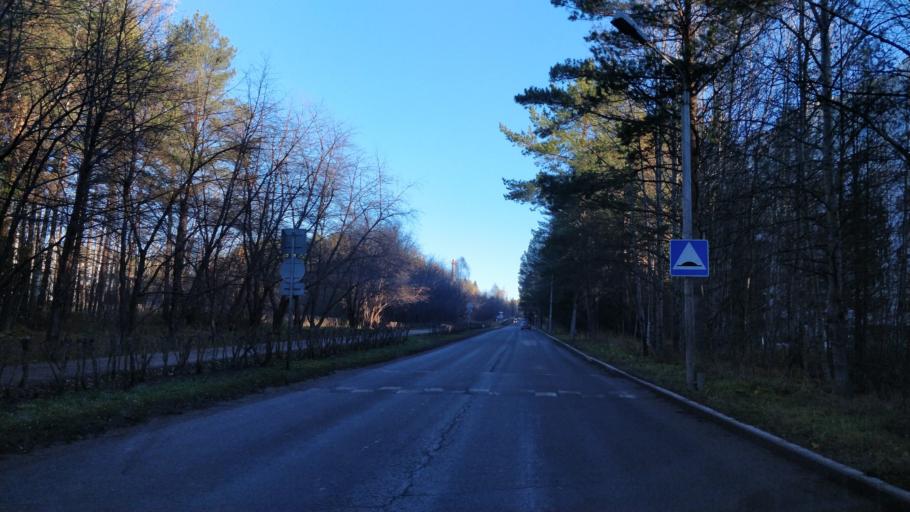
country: RU
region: Perm
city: Perm
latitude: 58.0499
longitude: 56.2135
